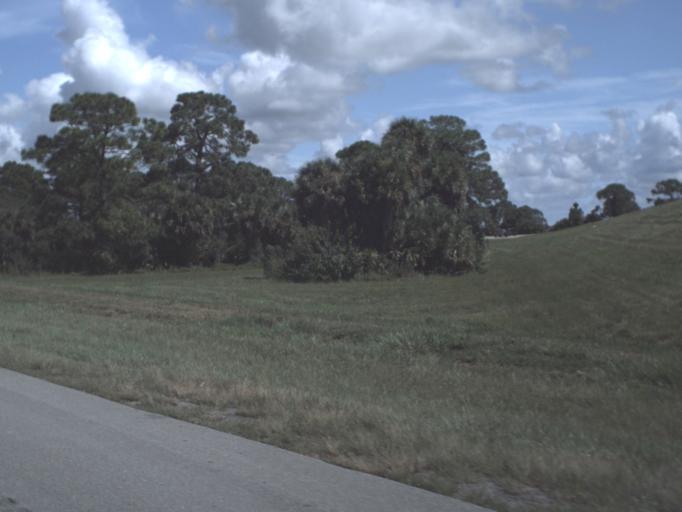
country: US
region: Florida
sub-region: Sarasota County
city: Osprey
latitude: 27.1918
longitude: -82.4380
